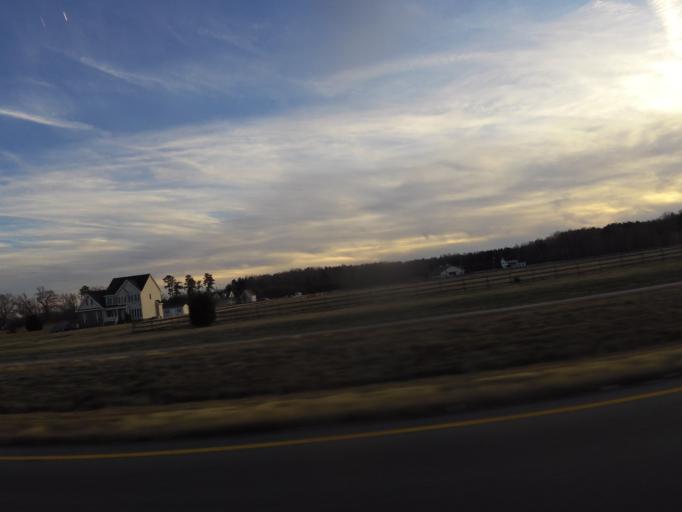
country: US
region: Virginia
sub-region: City of Franklin
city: Franklin
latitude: 36.6909
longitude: -76.9839
